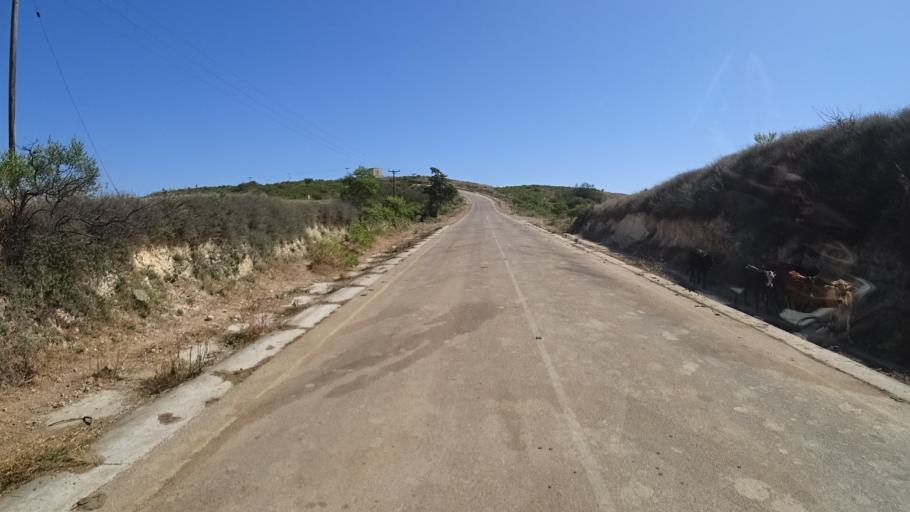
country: YE
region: Al Mahrah
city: Hawf
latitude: 16.7490
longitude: 53.3434
